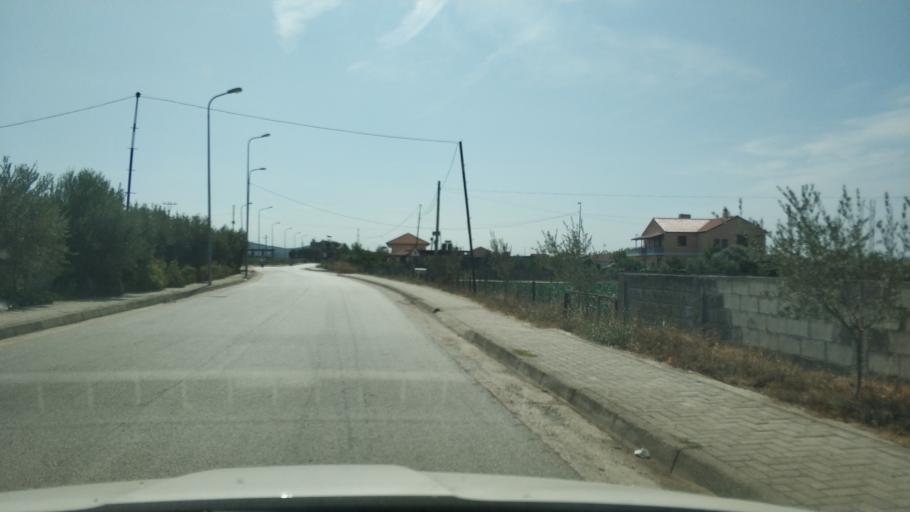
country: AL
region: Fier
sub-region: Rrethi i Lushnjes
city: Divjake
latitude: 40.9906
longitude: 19.5337
